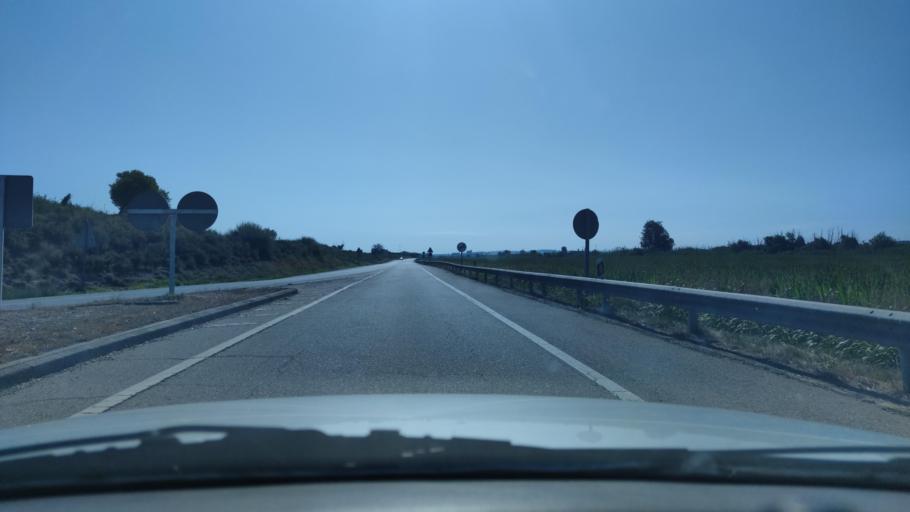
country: ES
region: Catalonia
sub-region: Provincia de Lleida
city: Alcoletge
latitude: 41.6290
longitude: 0.7511
